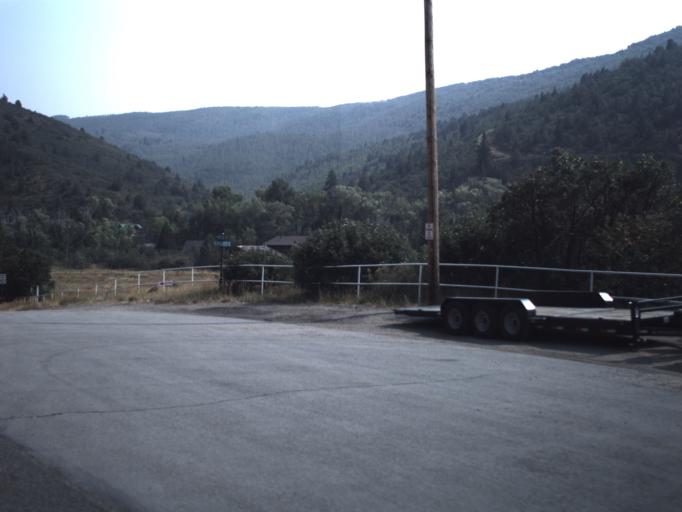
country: US
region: Utah
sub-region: Summit County
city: Francis
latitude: 40.6180
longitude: -111.2144
